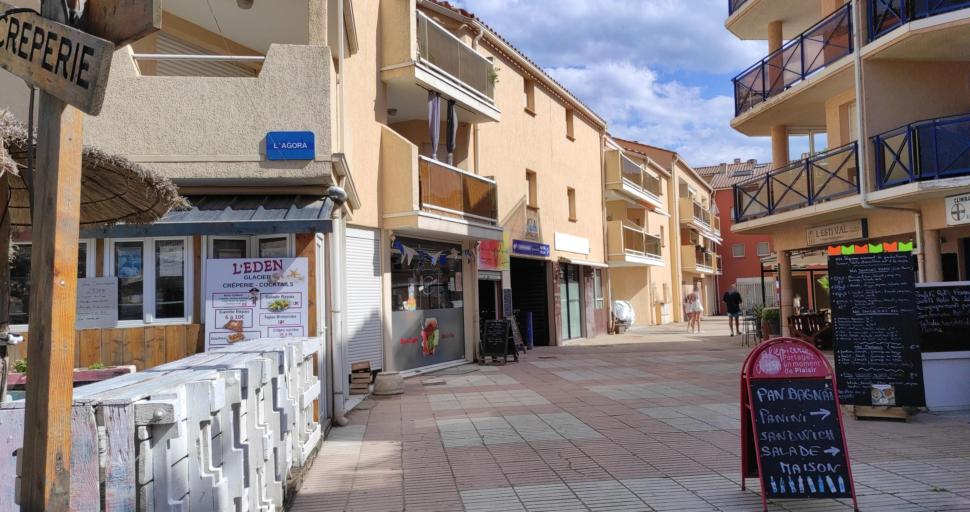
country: FR
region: Languedoc-Roussillon
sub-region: Departement des Pyrenees-Orientales
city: Sainte-Marie-Plage
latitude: 42.7347
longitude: 3.0366
